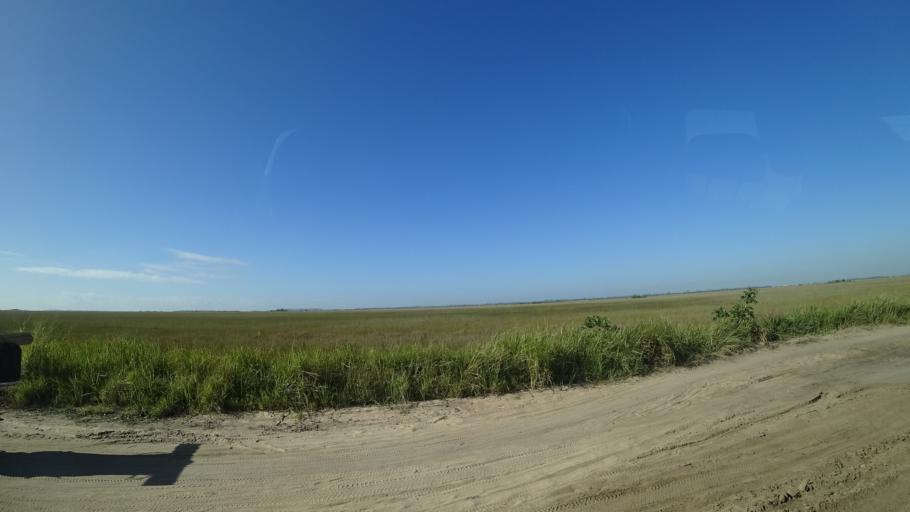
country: MZ
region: Sofala
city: Beira
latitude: -19.7546
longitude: 34.9275
